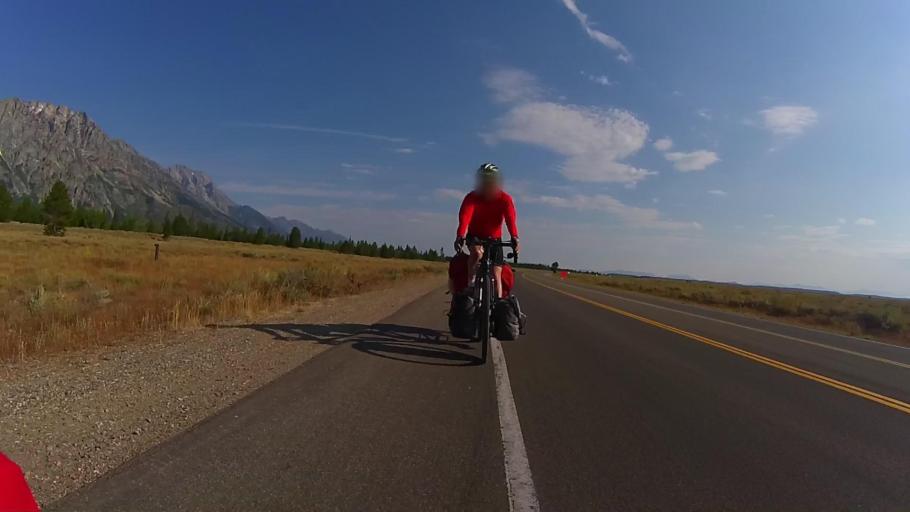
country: US
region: Wyoming
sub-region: Teton County
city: Moose Wilson Road
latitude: 43.7443
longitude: -110.7240
